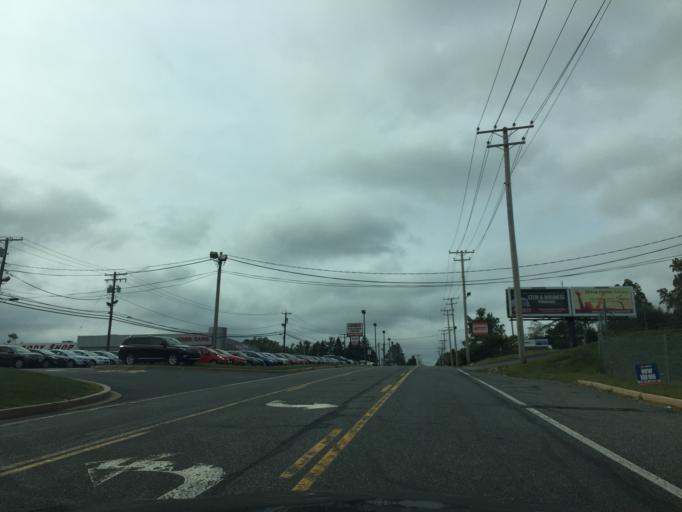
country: US
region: Maryland
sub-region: Harford County
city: Fallston
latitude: 39.5073
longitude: -76.3831
